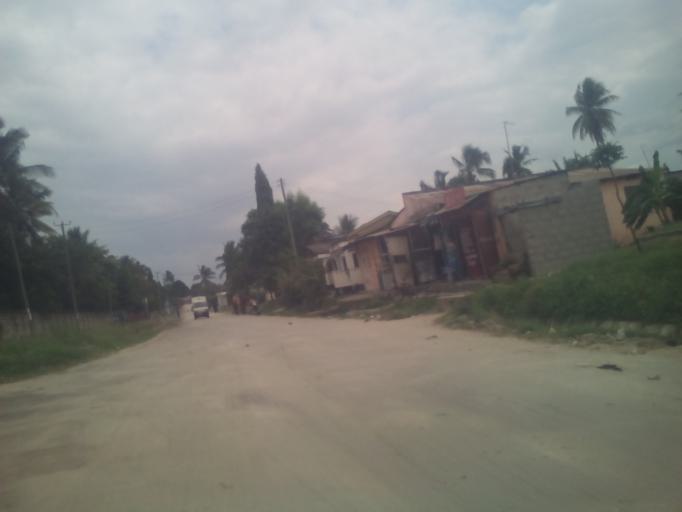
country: TZ
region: Dar es Salaam
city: Dar es Salaam
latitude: -6.8726
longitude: 39.2275
